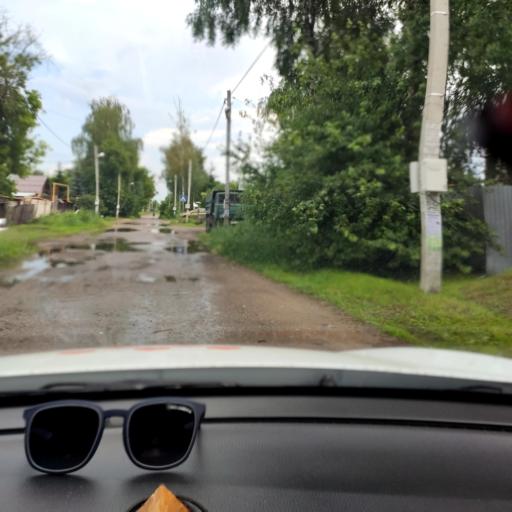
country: RU
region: Tatarstan
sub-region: Zelenodol'skiy Rayon
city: Vasil'yevo
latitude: 55.8291
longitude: 48.7102
